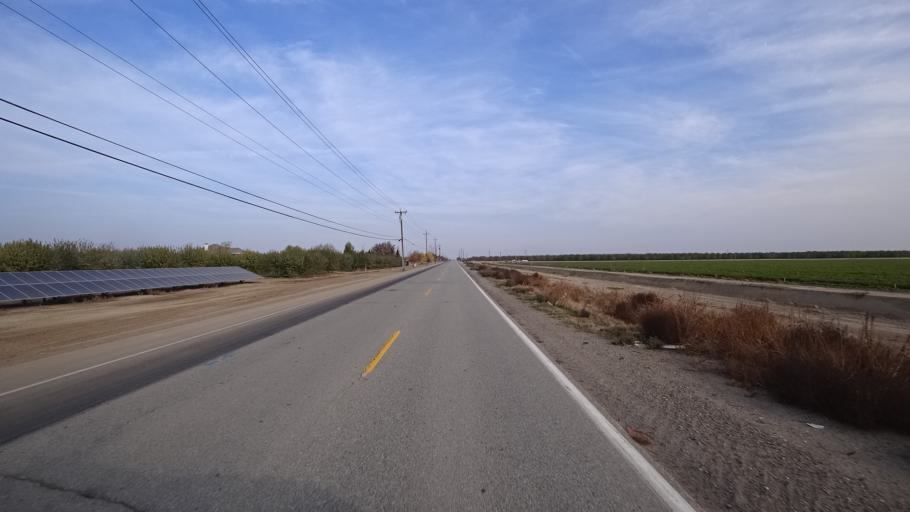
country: US
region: California
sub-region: Kern County
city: Rosedale
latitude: 35.2962
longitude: -119.1423
